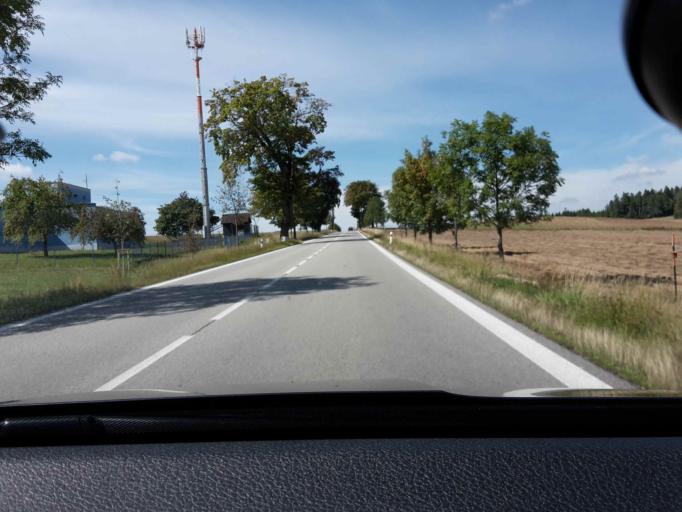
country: CZ
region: Jihocesky
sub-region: Okres Jindrichuv Hradec
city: Jindrichuv Hradec
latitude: 49.1617
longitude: 14.9430
